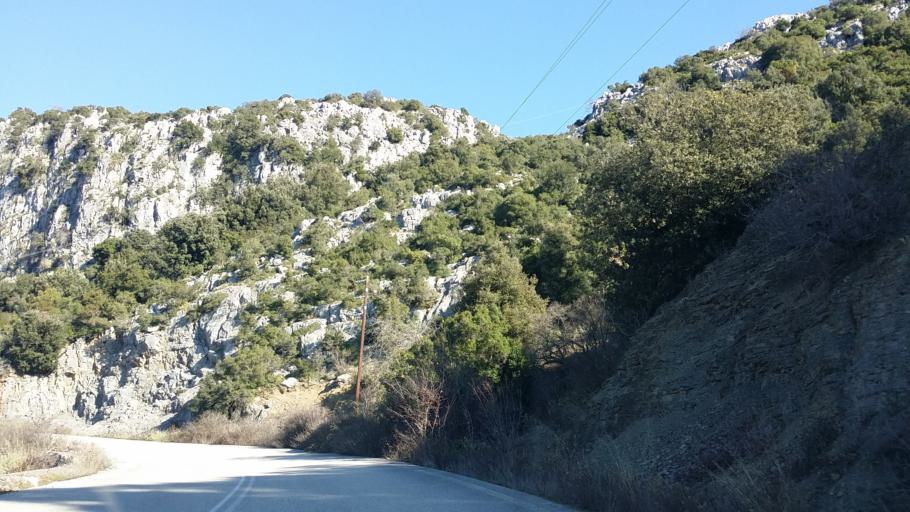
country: GR
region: West Greece
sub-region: Nomos Aitolias kai Akarnanias
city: Sardinia
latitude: 38.9219
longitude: 21.4067
